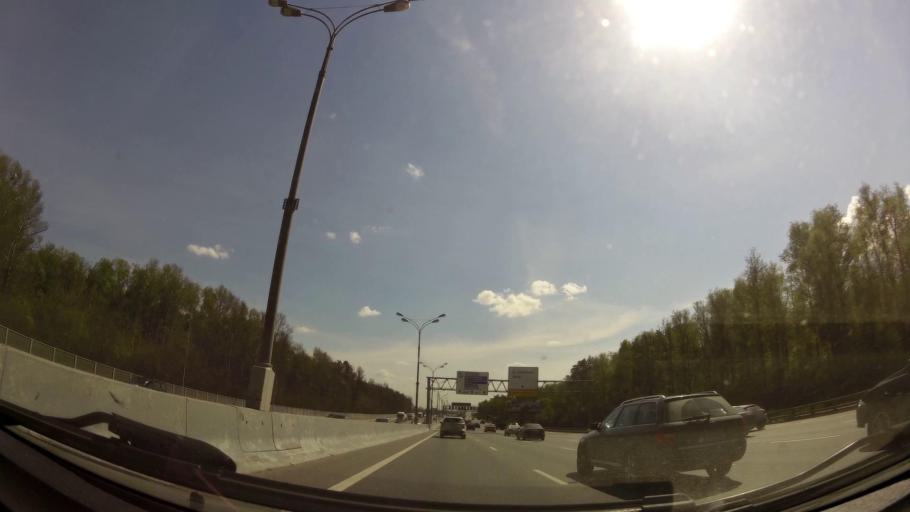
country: RU
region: Moskovskaya
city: Nemchinovka
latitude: 55.7424
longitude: 37.3711
